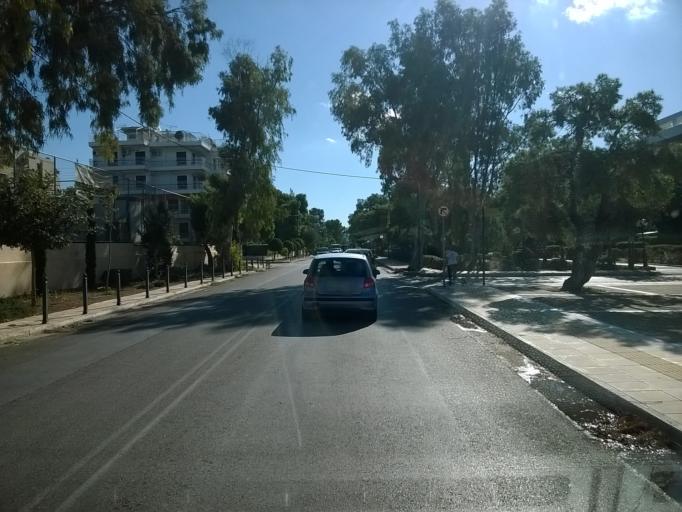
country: GR
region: Attica
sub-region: Nomarchia Anatolikis Attikis
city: Voula
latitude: 37.8449
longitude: 23.7610
